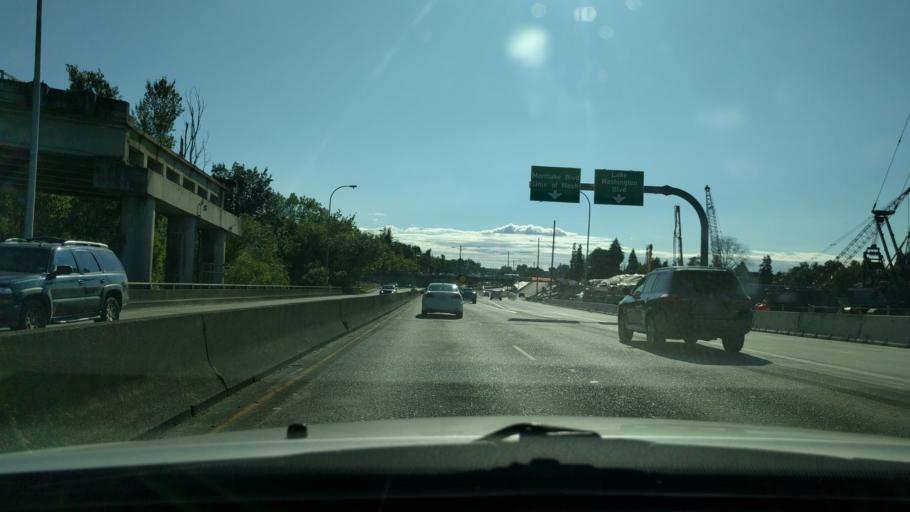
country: US
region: Washington
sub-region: King County
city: Seattle
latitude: 47.6451
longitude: -122.2972
